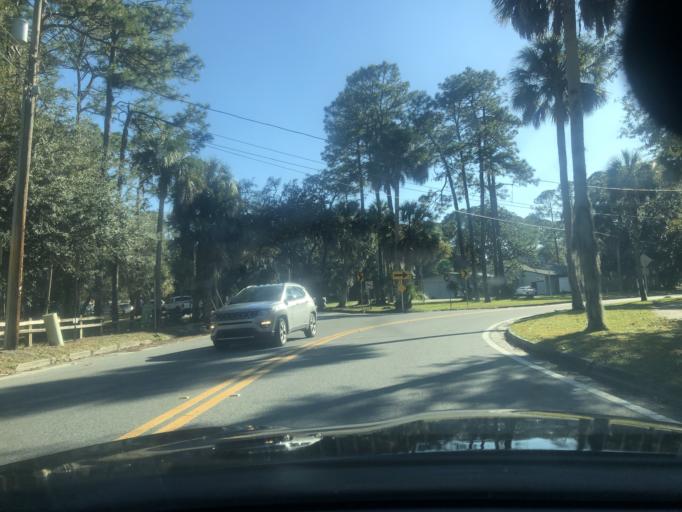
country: US
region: Florida
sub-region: Citrus County
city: Homosassa Springs
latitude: 28.8073
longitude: -82.5730
